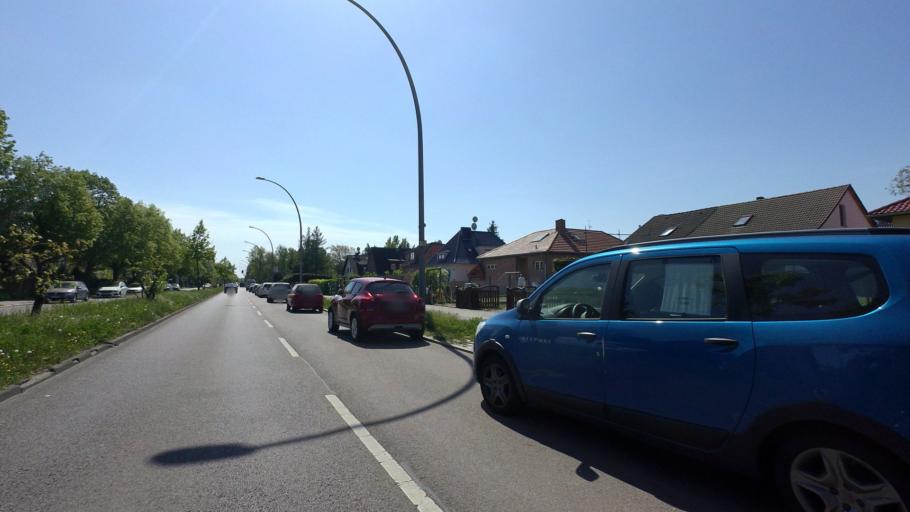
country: DE
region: Berlin
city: Rudow
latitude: 52.4110
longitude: 13.5041
